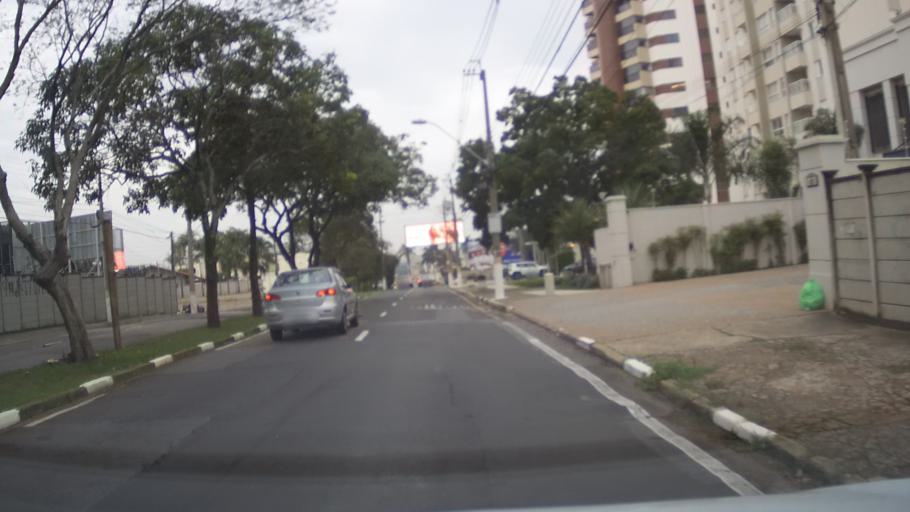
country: BR
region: Sao Paulo
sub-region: Campinas
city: Campinas
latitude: -22.8957
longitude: -47.0295
